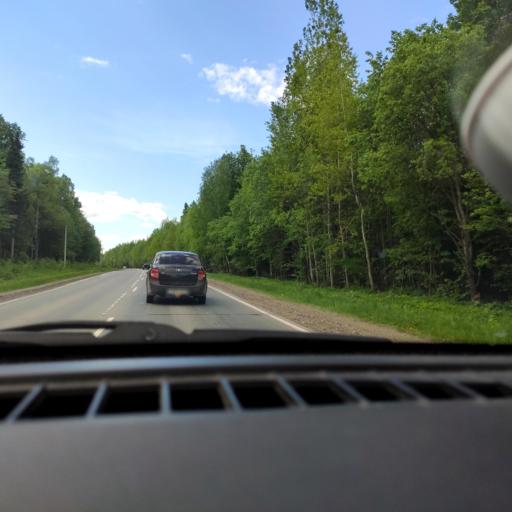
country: RU
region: Perm
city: Perm
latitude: 58.2057
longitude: 56.1981
